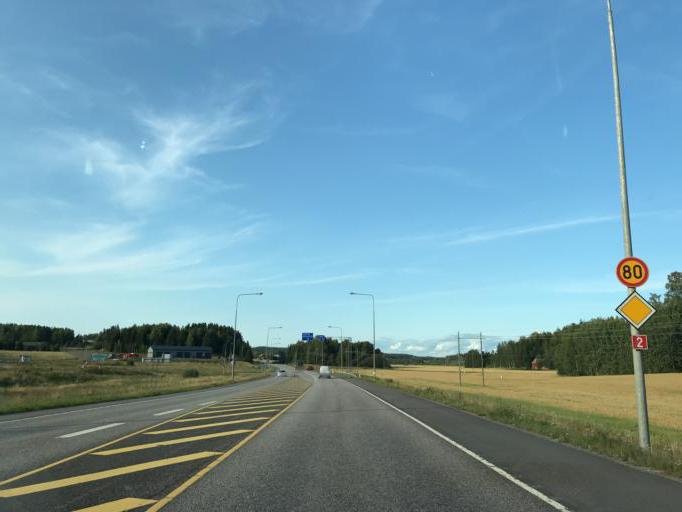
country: FI
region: Uusimaa
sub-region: Helsinki
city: Vihti
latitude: 60.3962
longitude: 24.3308
